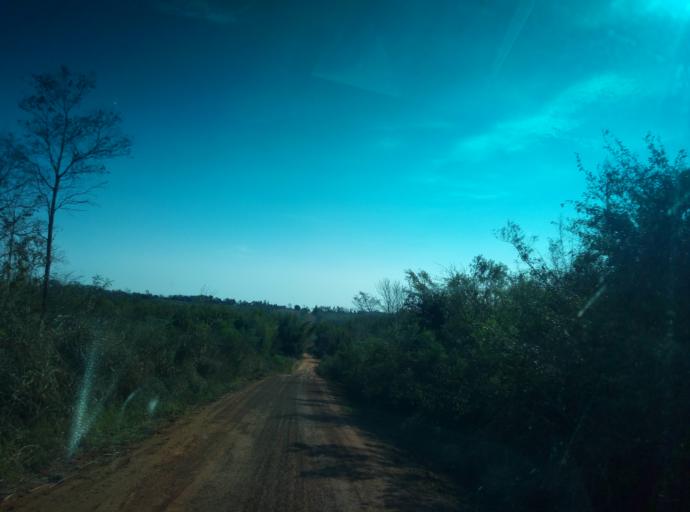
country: PY
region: Caaguazu
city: Doctor Cecilio Baez
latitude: -25.1648
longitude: -56.2209
